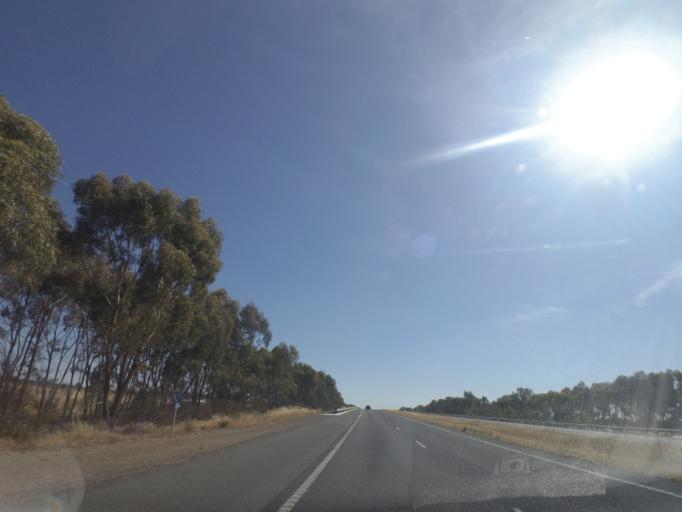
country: AU
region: Victoria
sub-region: Greater Shepparton
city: Shepparton
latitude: -36.6776
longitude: 145.2437
